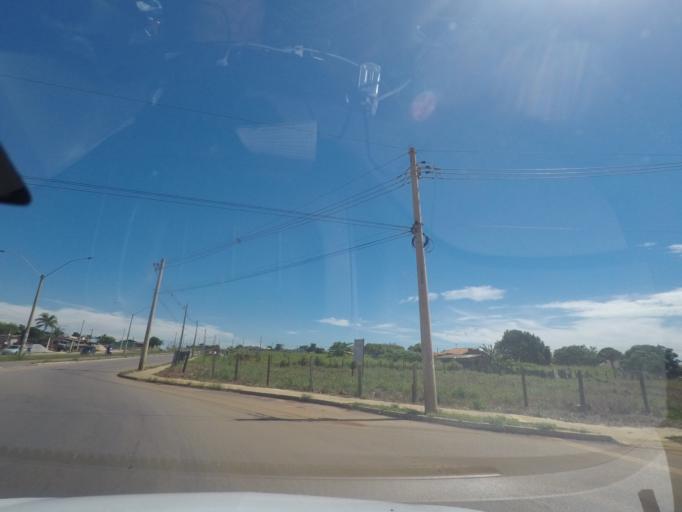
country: BR
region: Goias
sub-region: Aparecida De Goiania
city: Aparecida de Goiania
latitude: -16.7964
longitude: -49.3288
